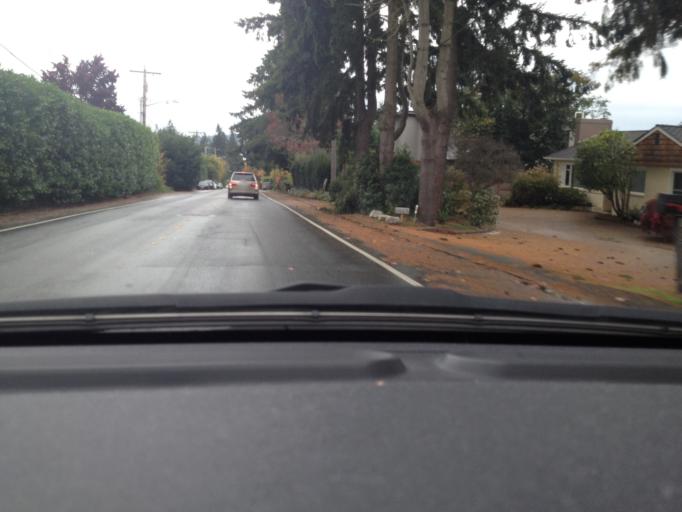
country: US
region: Washington
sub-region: King County
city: Medina
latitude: 47.6211
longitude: -122.2179
